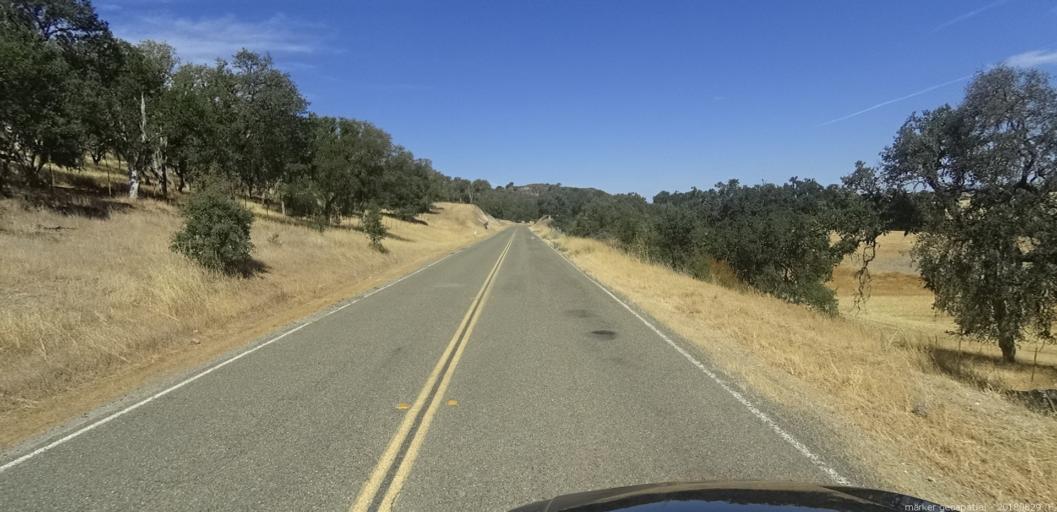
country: US
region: California
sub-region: San Luis Obispo County
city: Lake Nacimiento
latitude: 35.8118
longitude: -121.0042
